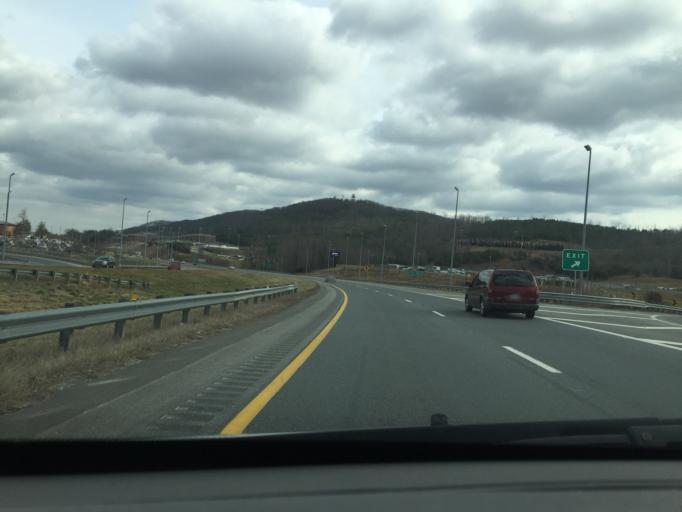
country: US
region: Virginia
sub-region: City of Lynchburg
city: West Lynchburg
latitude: 37.3404
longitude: -79.1878
